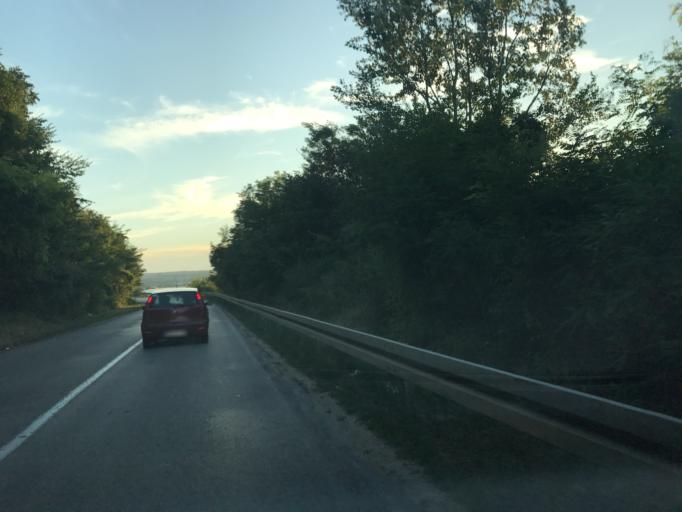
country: RS
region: Central Serbia
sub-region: Branicevski Okrug
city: Golubac
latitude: 44.6573
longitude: 21.6581
